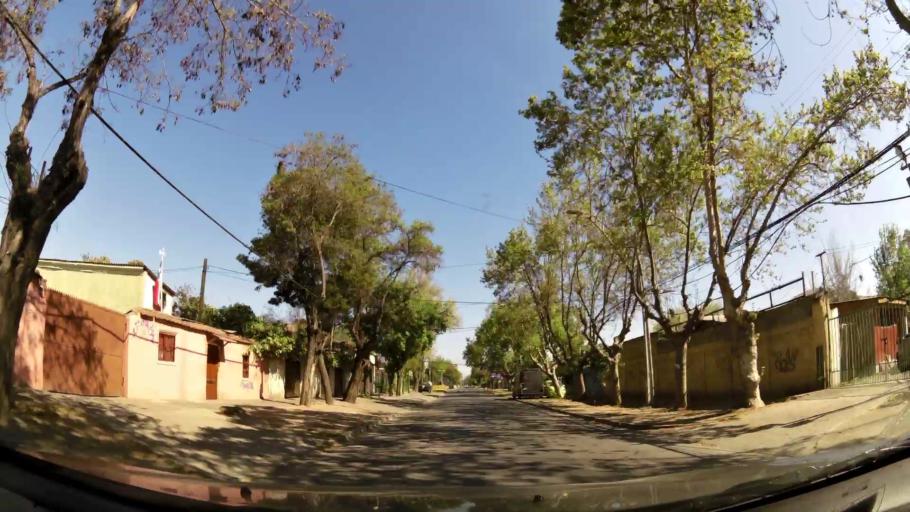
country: CL
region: Santiago Metropolitan
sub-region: Provincia de Maipo
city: San Bernardo
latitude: -33.5971
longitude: -70.7117
